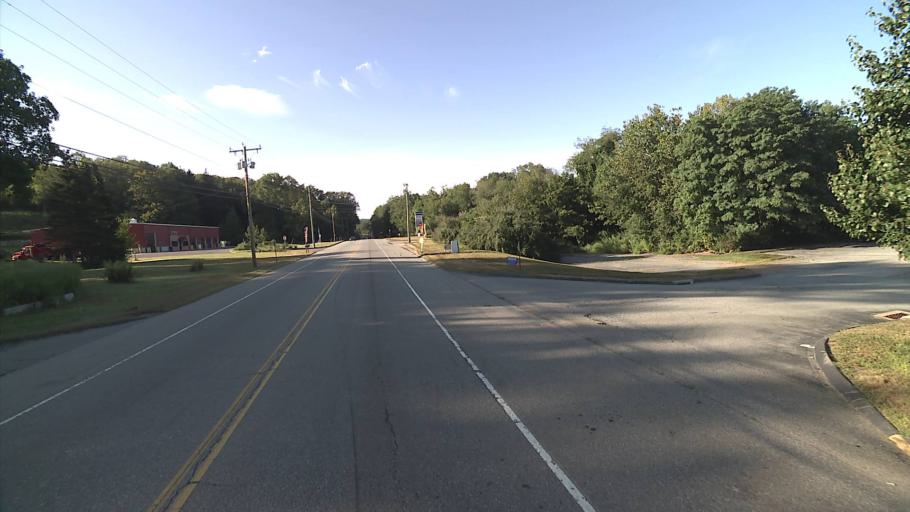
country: US
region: Connecticut
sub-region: New London County
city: Baltic
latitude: 41.5756
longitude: -72.1317
